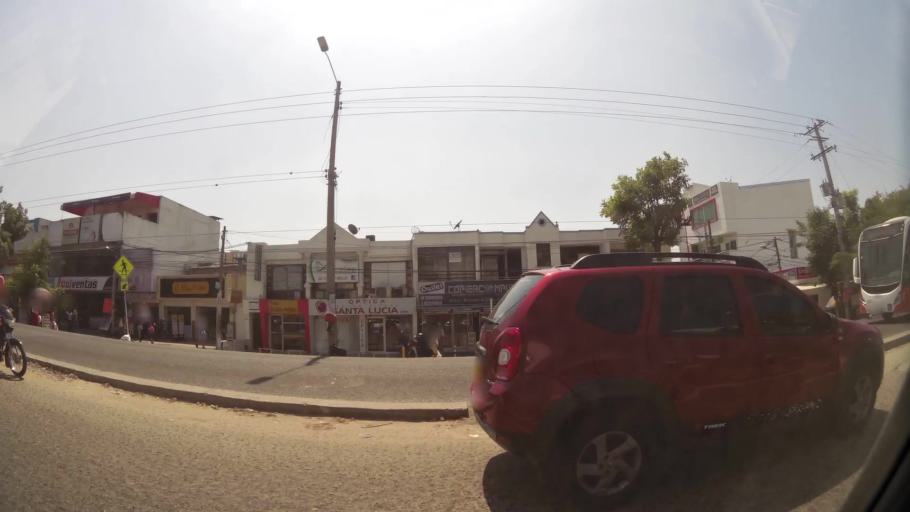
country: CO
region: Bolivar
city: Cartagena
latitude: 10.3916
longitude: -75.4802
